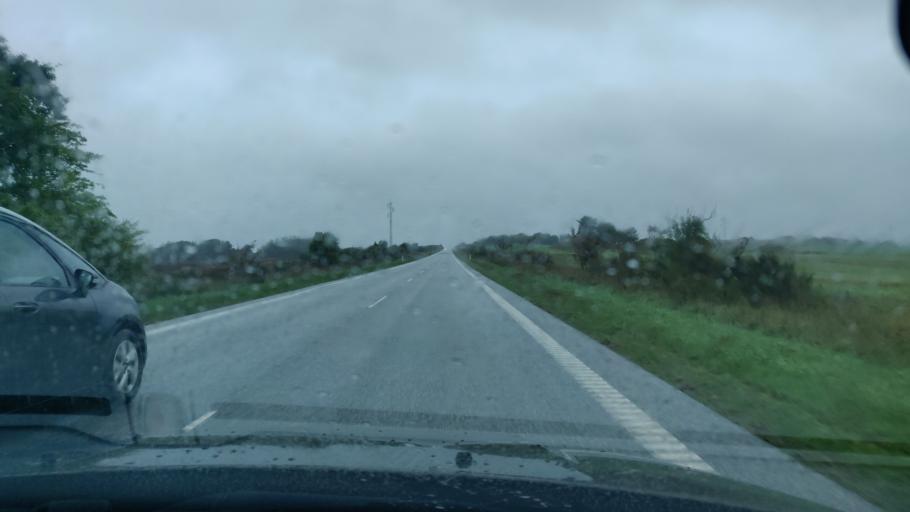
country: DK
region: North Denmark
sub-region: Thisted Kommune
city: Hurup
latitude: 56.8105
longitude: 8.4830
